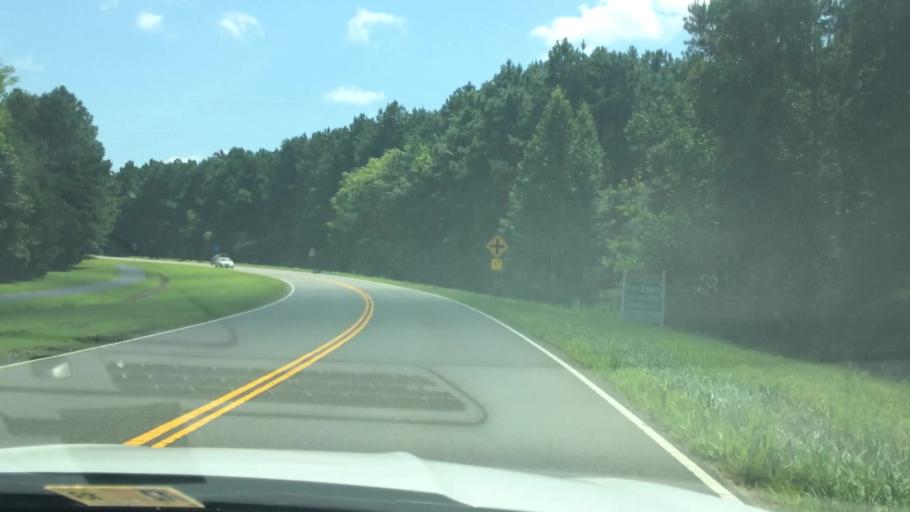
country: US
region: Virginia
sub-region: James City County
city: Williamsburg
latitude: 37.2968
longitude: -76.7403
